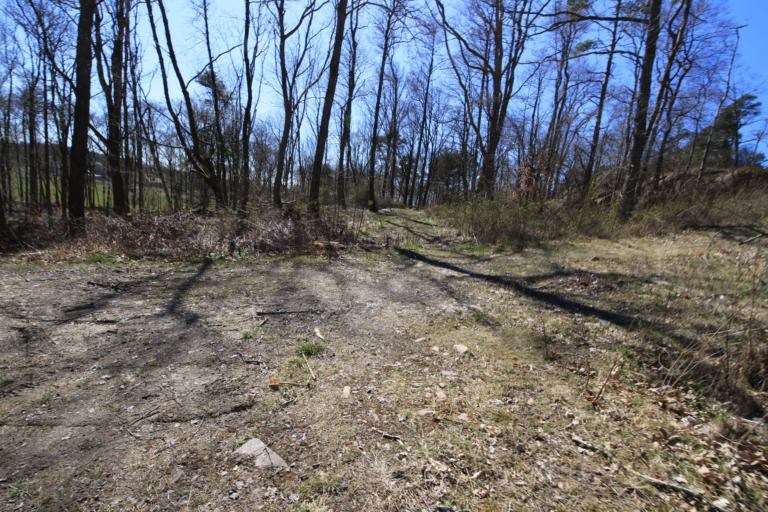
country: SE
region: Halland
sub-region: Varbergs Kommun
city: Varberg
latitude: 57.1633
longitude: 12.2615
